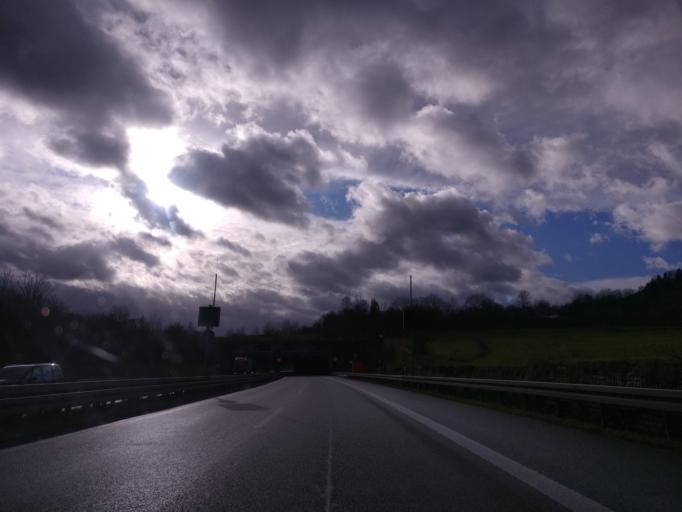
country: DE
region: Baden-Wuerttemberg
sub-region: Regierungsbezirk Stuttgart
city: Schorndorf
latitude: 48.8187
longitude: 9.5195
